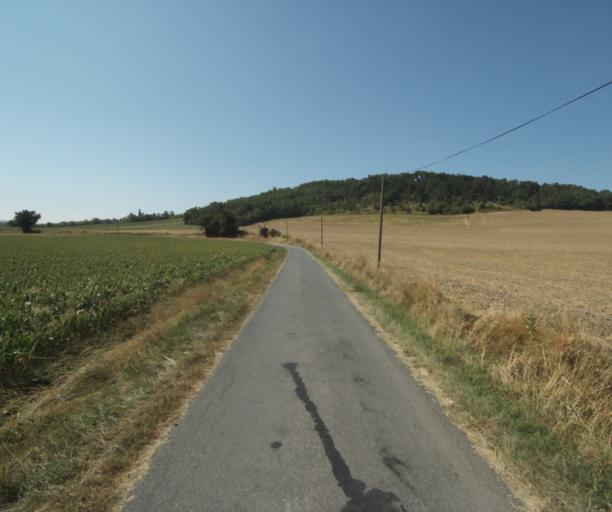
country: FR
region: Midi-Pyrenees
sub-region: Departement de la Haute-Garonne
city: Revel
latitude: 43.5161
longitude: 1.9487
